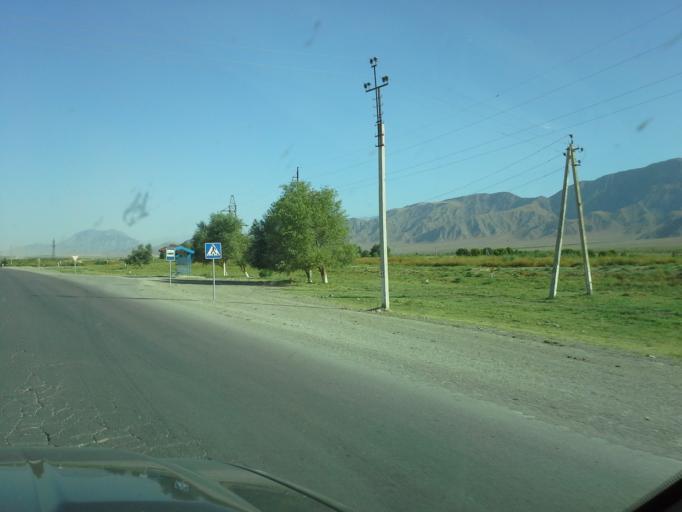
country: TM
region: Ahal
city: Arcabil
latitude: 38.1980
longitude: 57.8293
